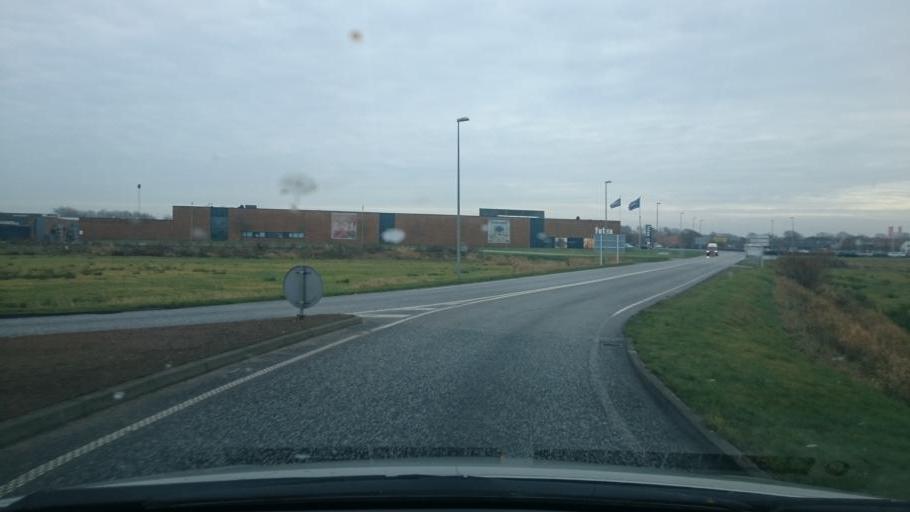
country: DK
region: South Denmark
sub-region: Esbjerg Kommune
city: Ribe
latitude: 55.3348
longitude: 8.7677
